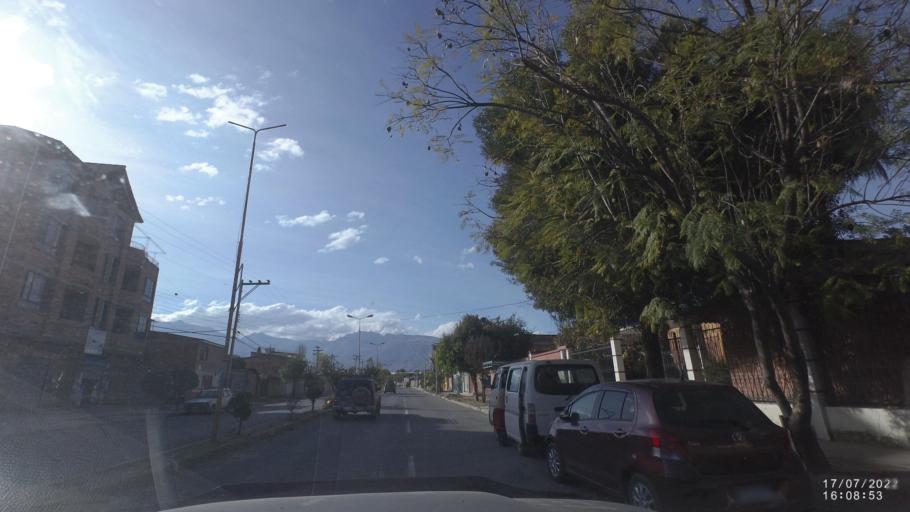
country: BO
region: Cochabamba
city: Cochabamba
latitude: -17.4048
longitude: -66.2734
